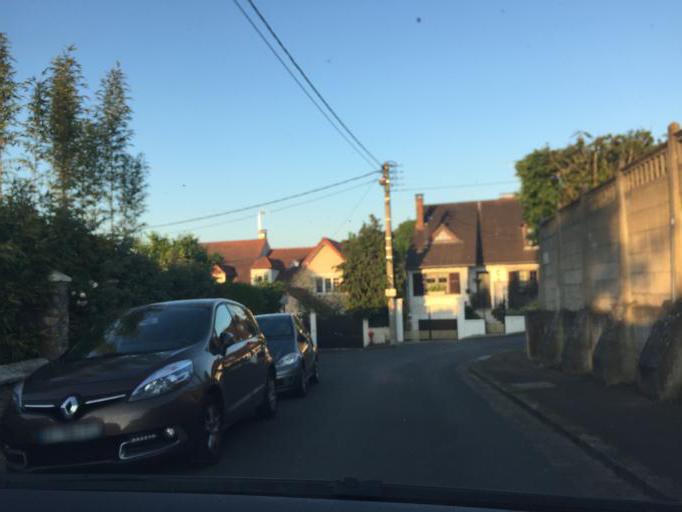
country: FR
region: Ile-de-France
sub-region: Departement de l'Essonne
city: Orsay
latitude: 48.7008
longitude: 2.2069
